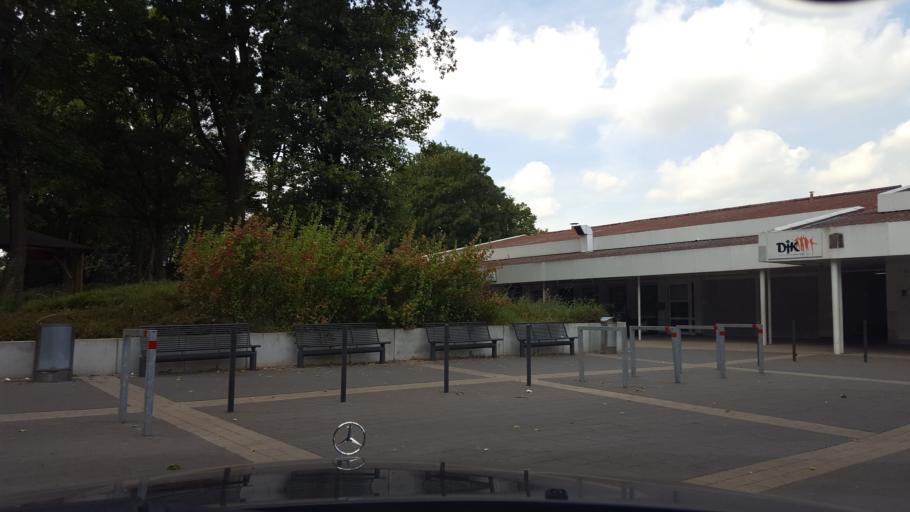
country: DE
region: North Rhine-Westphalia
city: Marl
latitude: 51.6582
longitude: 7.1438
